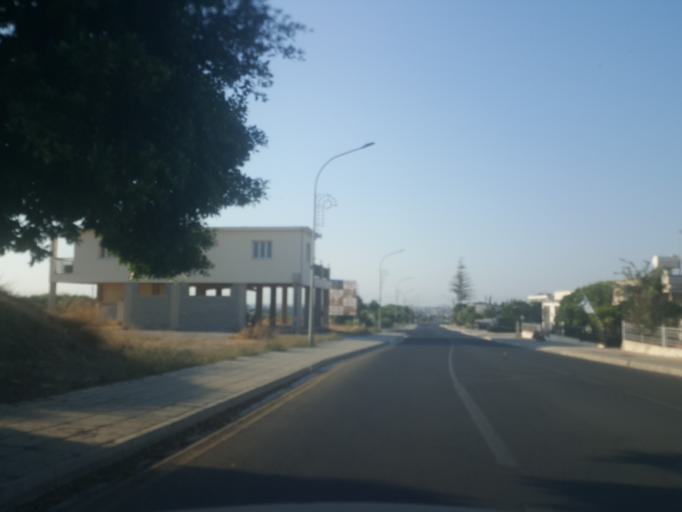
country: CY
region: Ammochostos
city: Deryneia
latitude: 35.0696
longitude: 33.9607
